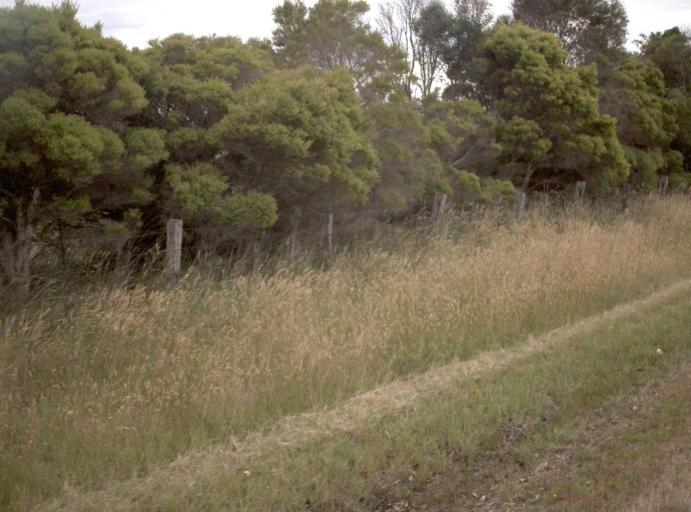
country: AU
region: Victoria
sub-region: East Gippsland
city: Bairnsdale
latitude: -37.9555
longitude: 147.5069
